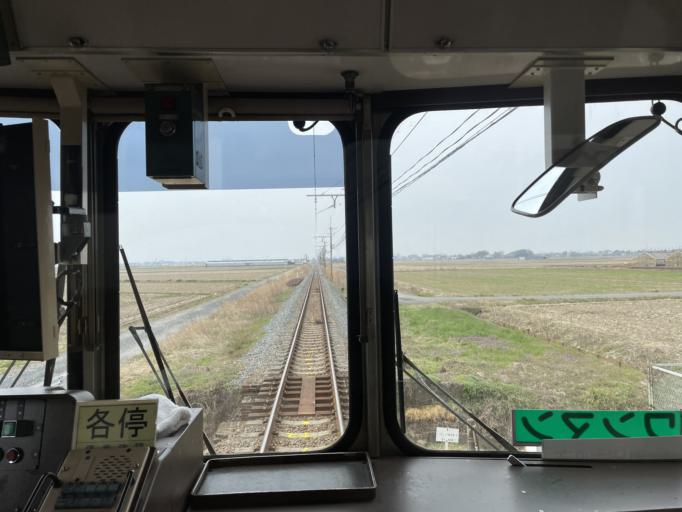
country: JP
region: Saitama
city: Hanyu
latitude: 36.1700
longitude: 139.5074
